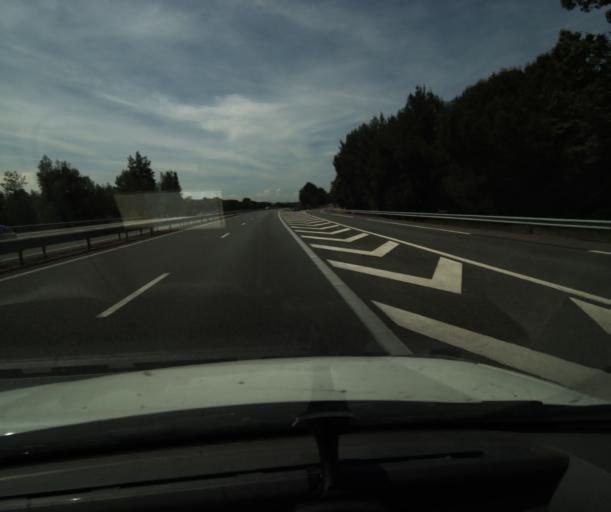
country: FR
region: Languedoc-Roussillon
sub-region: Departement de l'Aude
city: Bram
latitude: 43.2281
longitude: 2.1182
